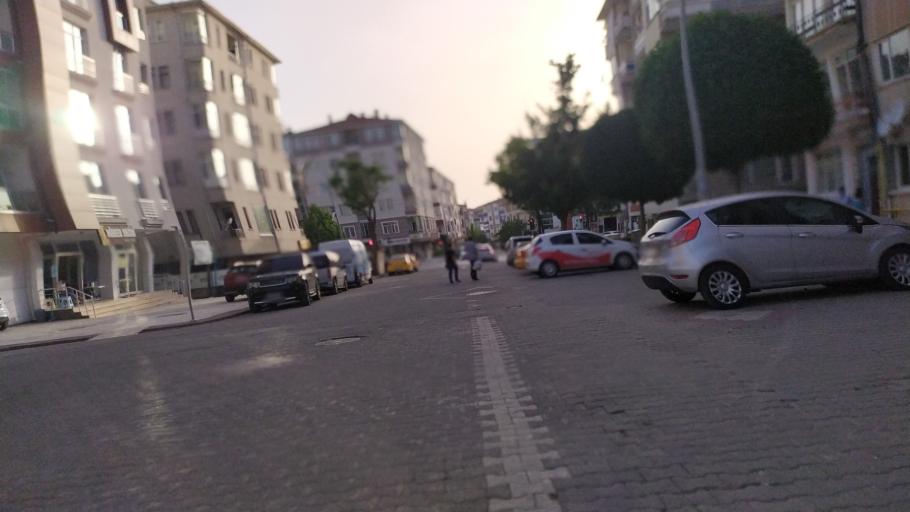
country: TR
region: Kirsehir
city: Kirsehir
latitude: 39.1520
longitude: 34.1604
